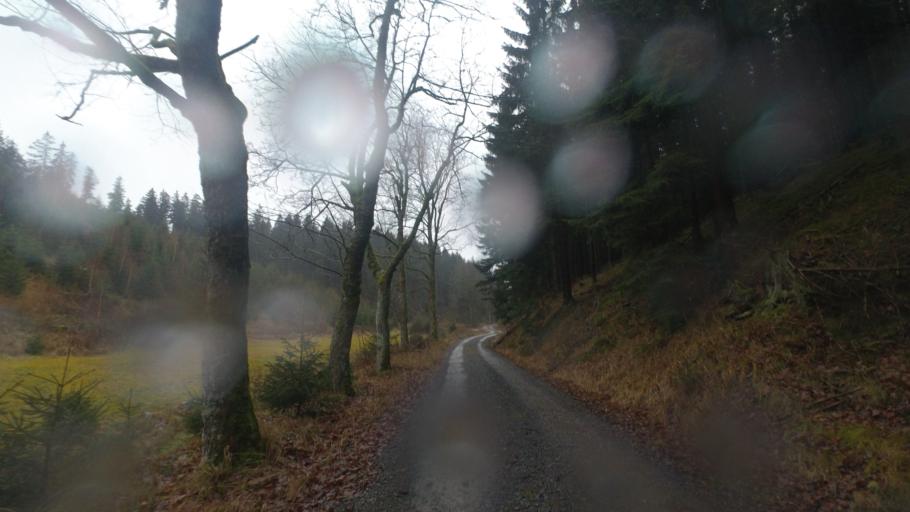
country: DE
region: Thuringia
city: Frankenhain
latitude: 50.7147
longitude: 10.7666
